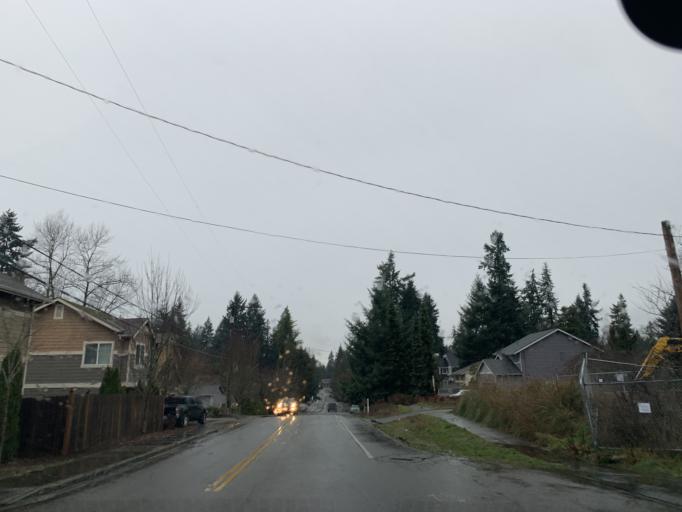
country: US
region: Washington
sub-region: King County
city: Kingsgate
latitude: 47.7258
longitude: -122.1705
